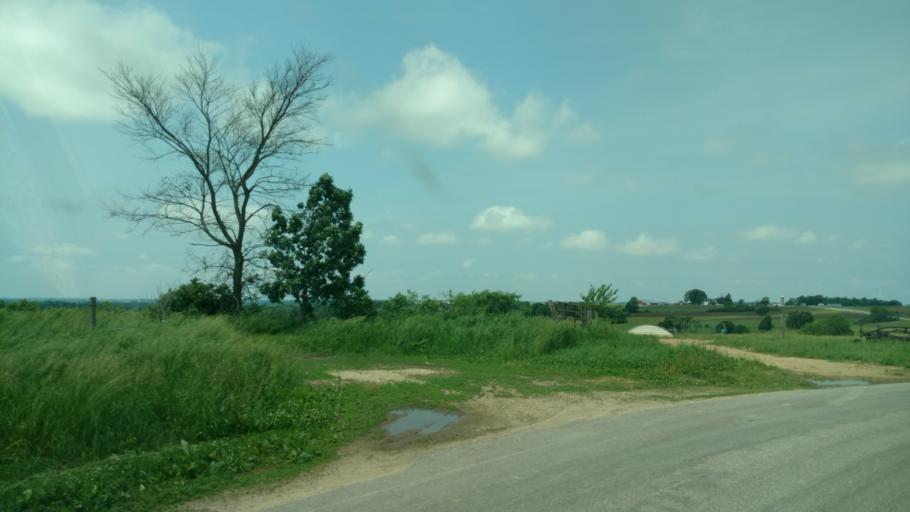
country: US
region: Wisconsin
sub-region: Monroe County
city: Cashton
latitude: 43.7147
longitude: -90.7201
